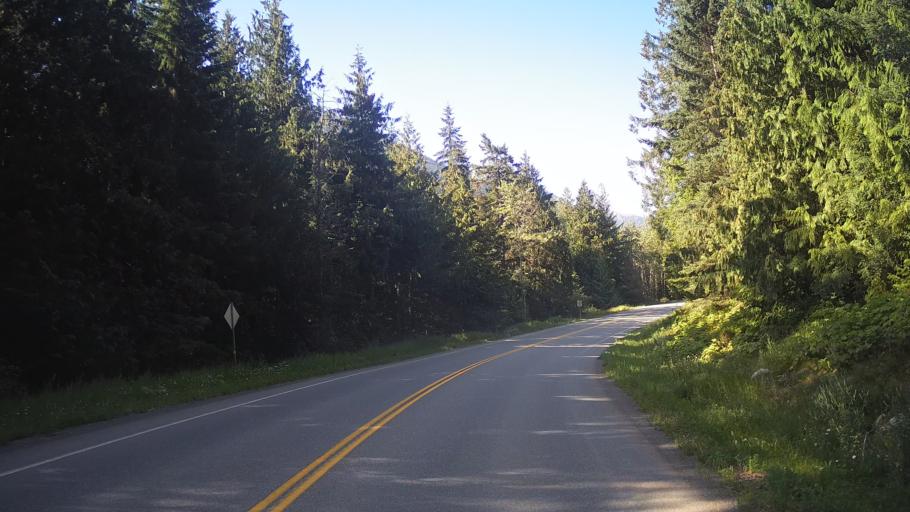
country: CA
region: British Columbia
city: Lillooet
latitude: 50.5307
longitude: -122.1557
